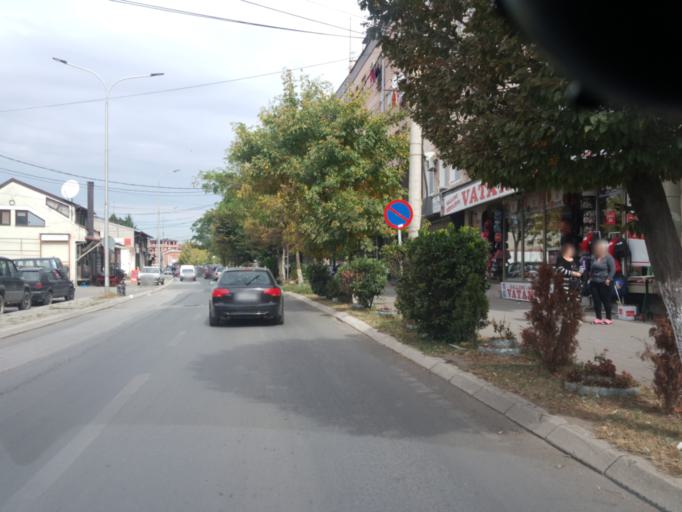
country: XK
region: Gjakova
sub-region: Komuna e Gjakoves
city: Gjakove
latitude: 42.3870
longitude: 20.4278
